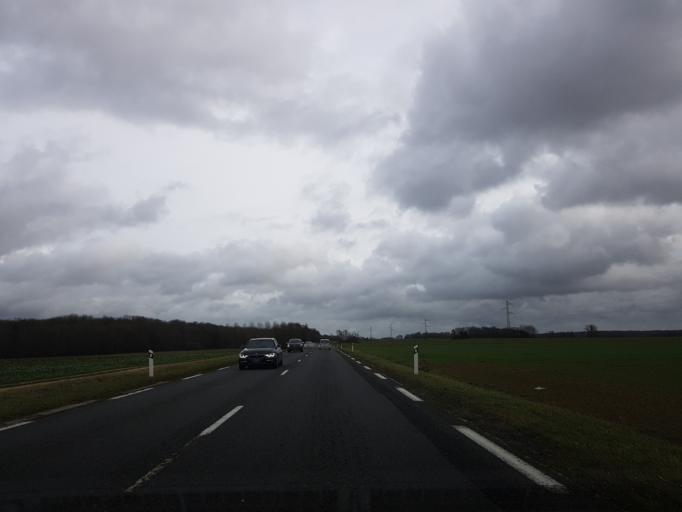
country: FR
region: Champagne-Ardenne
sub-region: Departement de la Haute-Marne
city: Chalindrey
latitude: 47.8142
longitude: 5.5087
